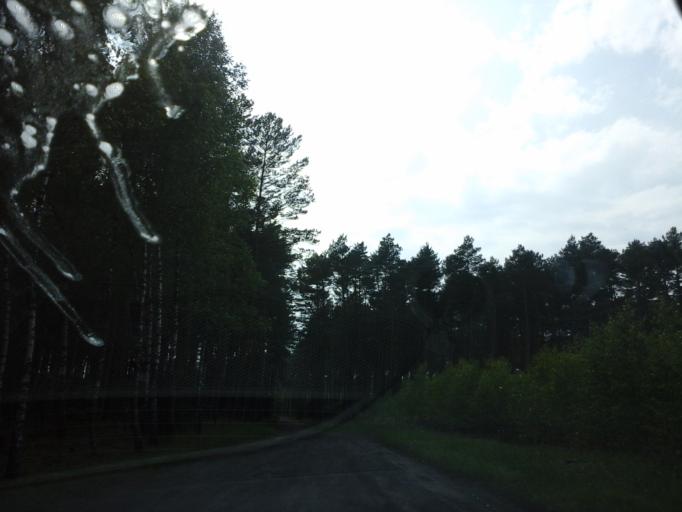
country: PL
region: West Pomeranian Voivodeship
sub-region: Powiat walecki
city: Tuczno
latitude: 53.2208
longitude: 16.0293
